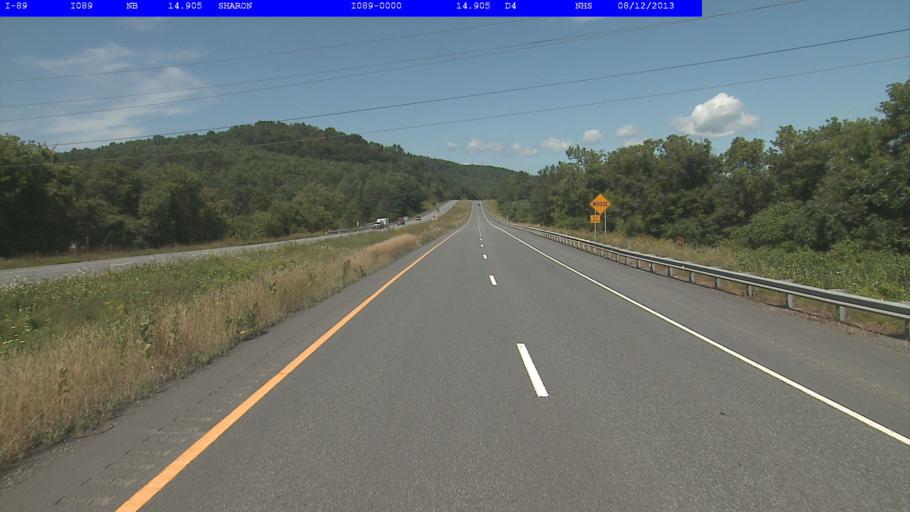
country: US
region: Vermont
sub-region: Windsor County
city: Woodstock
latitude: 43.7824
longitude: -72.4809
